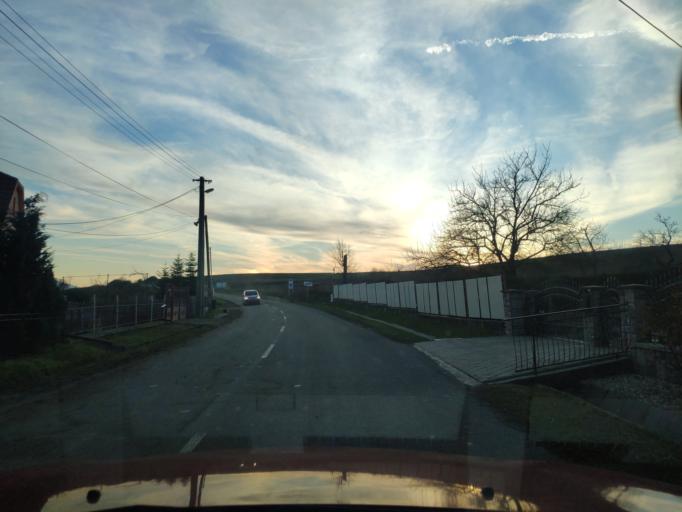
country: SK
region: Kosicky
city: Kosice
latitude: 48.7023
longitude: 21.4118
